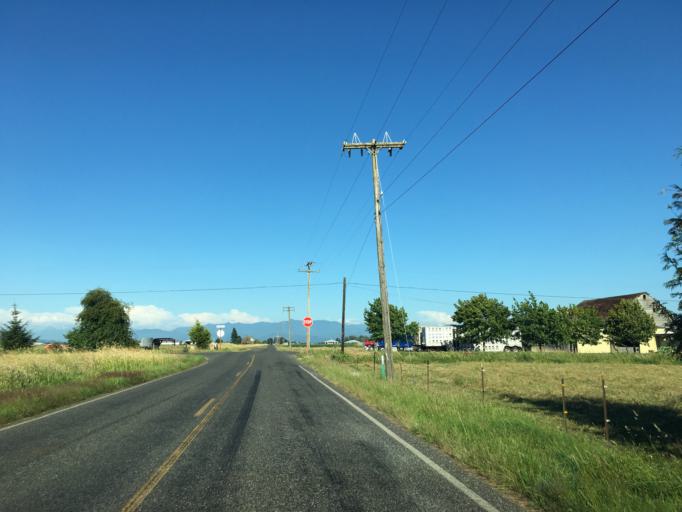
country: US
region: Washington
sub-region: Whatcom County
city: Lynden
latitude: 48.9863
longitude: -122.4748
